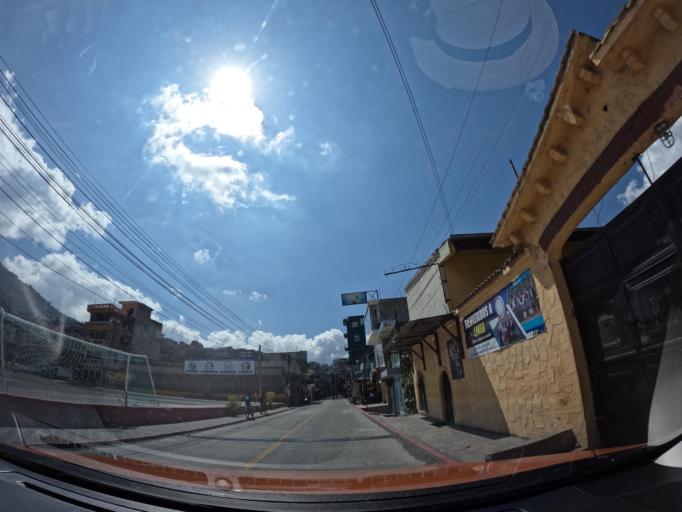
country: GT
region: Solola
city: Santiago Atitlan
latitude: 14.6439
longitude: -91.2272
